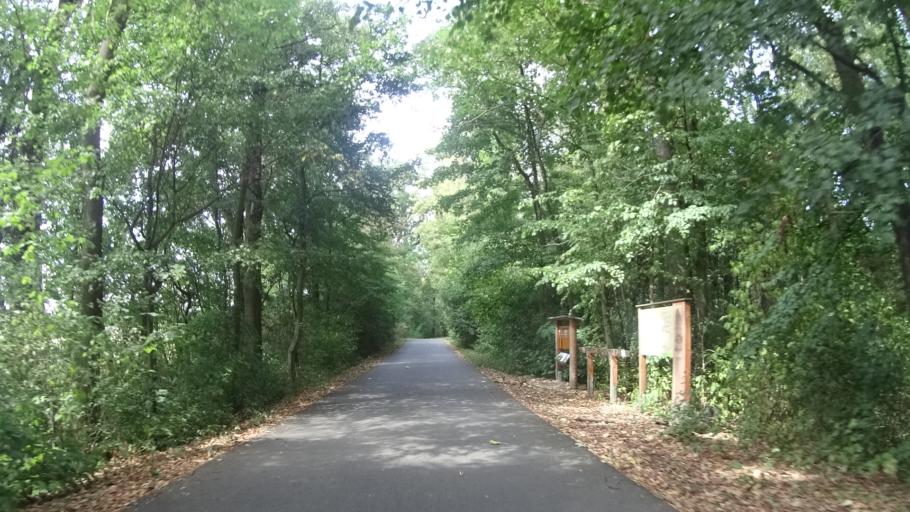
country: CZ
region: Olomoucky
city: Horka nad Moravou
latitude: 49.6508
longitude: 17.1949
